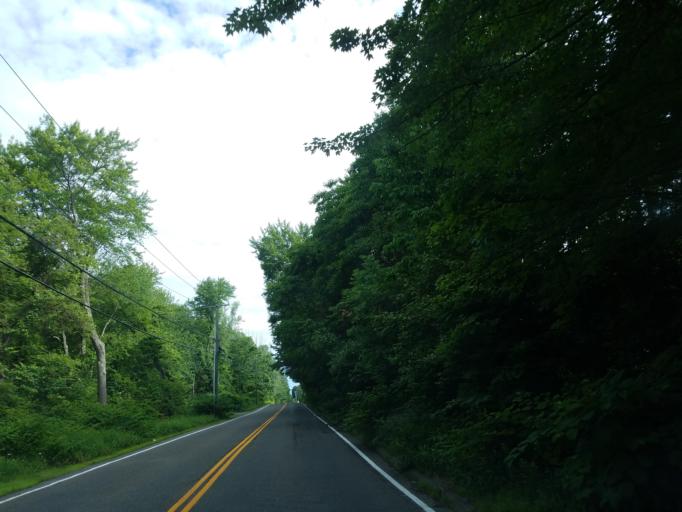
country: US
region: Connecticut
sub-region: Litchfield County
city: Plymouth
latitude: 41.6314
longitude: -73.0501
